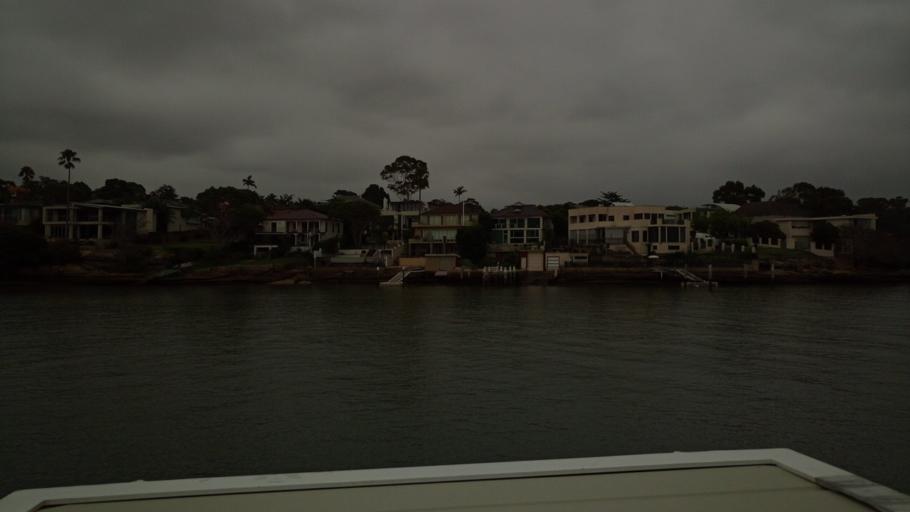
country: AU
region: New South Wales
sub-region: Canada Bay
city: Canada Bay
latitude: -33.8458
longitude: 151.1375
